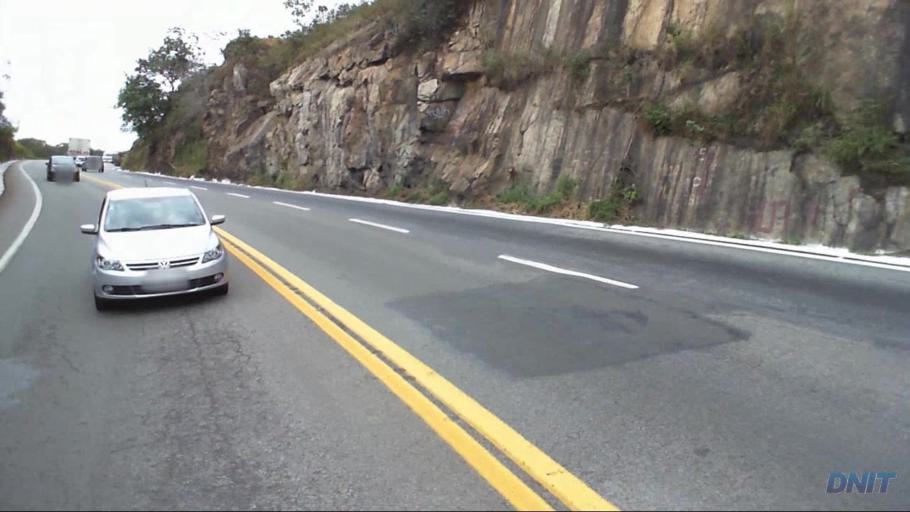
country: BR
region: Minas Gerais
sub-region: Caete
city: Caete
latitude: -19.7868
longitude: -43.7174
